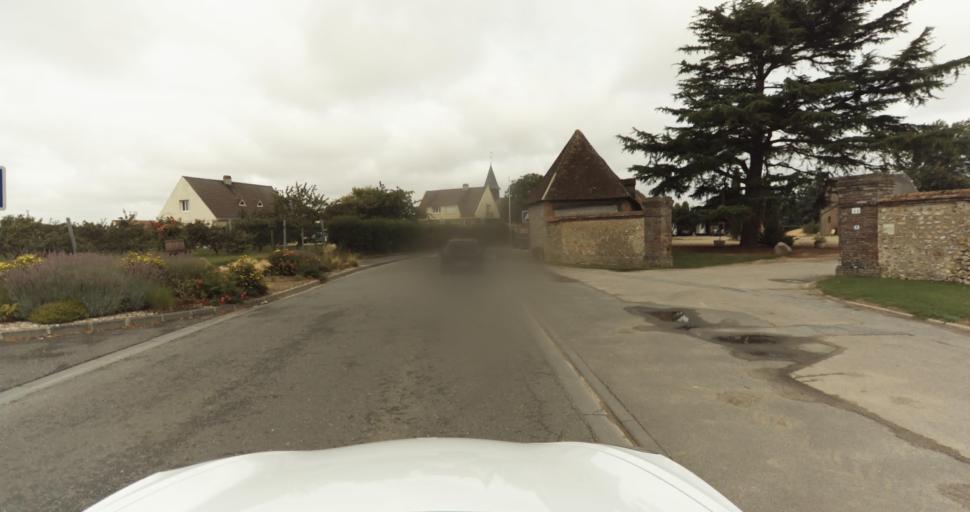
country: FR
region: Haute-Normandie
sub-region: Departement de l'Eure
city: Aviron
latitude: 49.0514
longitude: 1.0860
